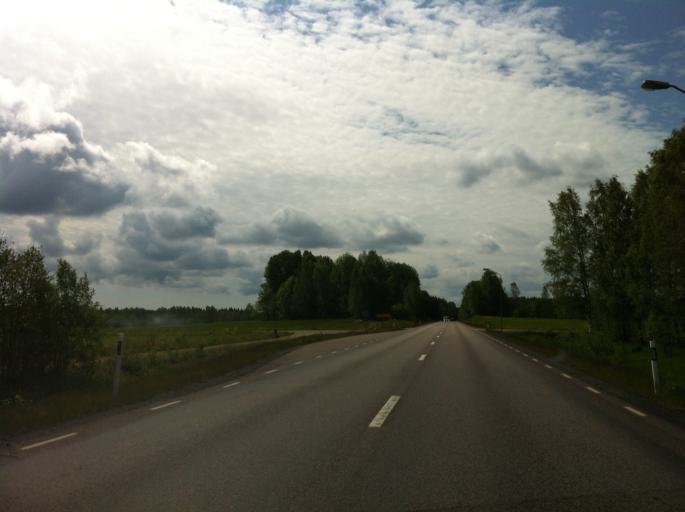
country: SE
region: Vaermland
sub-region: Karlstads Kommun
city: Edsvalla
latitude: 59.4739
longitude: 13.2159
